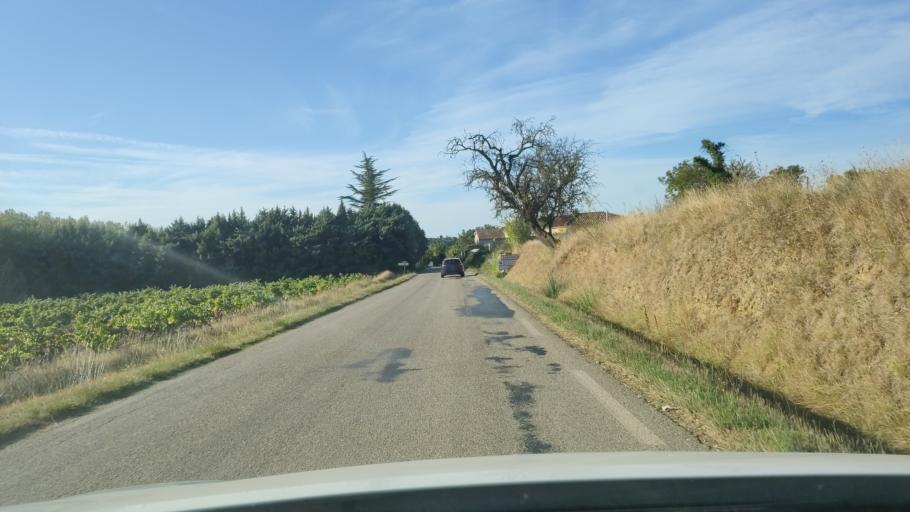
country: FR
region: Languedoc-Roussillon
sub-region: Departement du Gard
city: Saze
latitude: 43.9365
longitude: 4.6522
